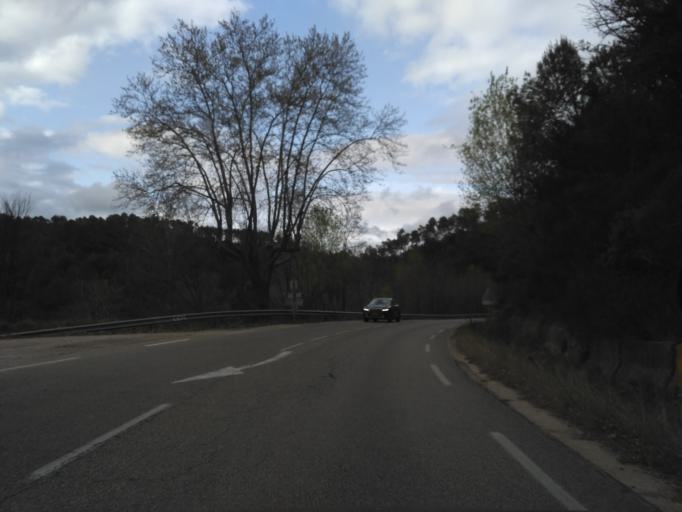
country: FR
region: Provence-Alpes-Cote d'Azur
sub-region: Departement du Var
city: Barjols
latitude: 43.5681
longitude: 6.0120
